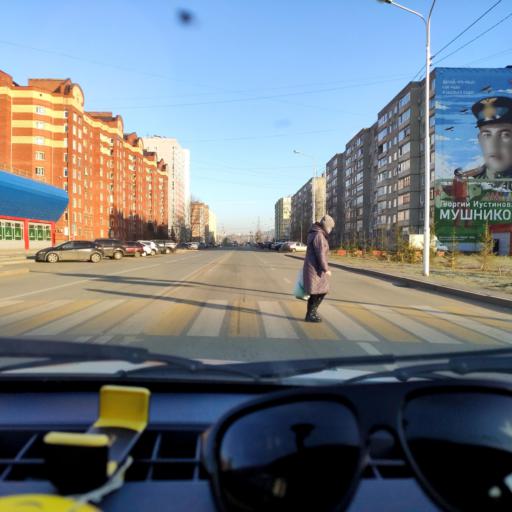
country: RU
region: Bashkortostan
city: Ufa
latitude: 54.7804
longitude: 56.1155
